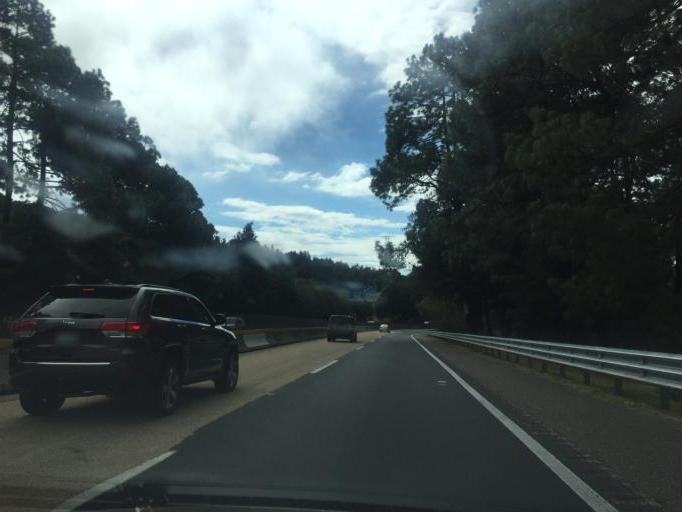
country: MX
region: Morelos
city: Tres Marias
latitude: 19.0672
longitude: -99.2383
